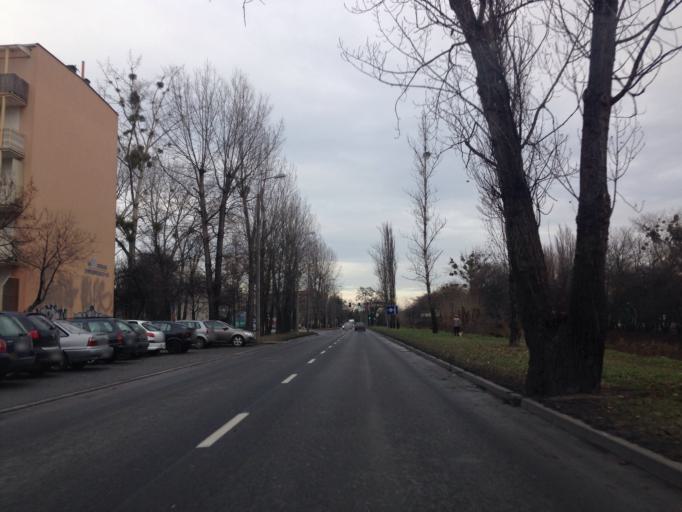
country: PL
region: Kujawsko-Pomorskie
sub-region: Torun
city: Torun
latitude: 53.0183
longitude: 18.6207
